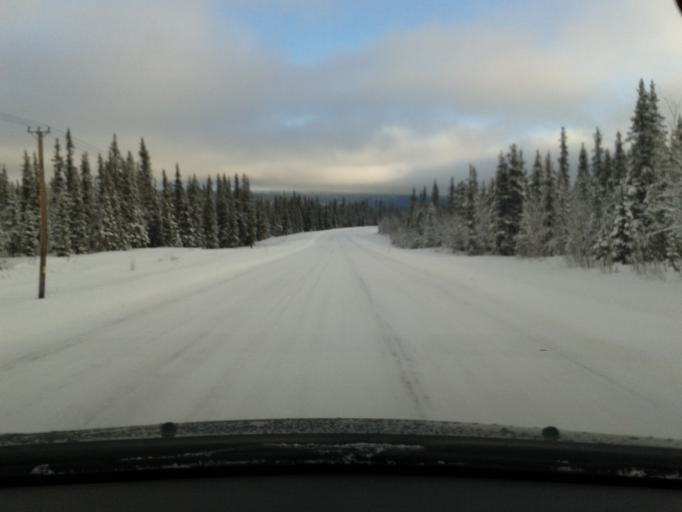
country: SE
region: Vaesterbotten
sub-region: Vilhelmina Kommun
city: Sjoberg
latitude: 65.2561
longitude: 15.6497
